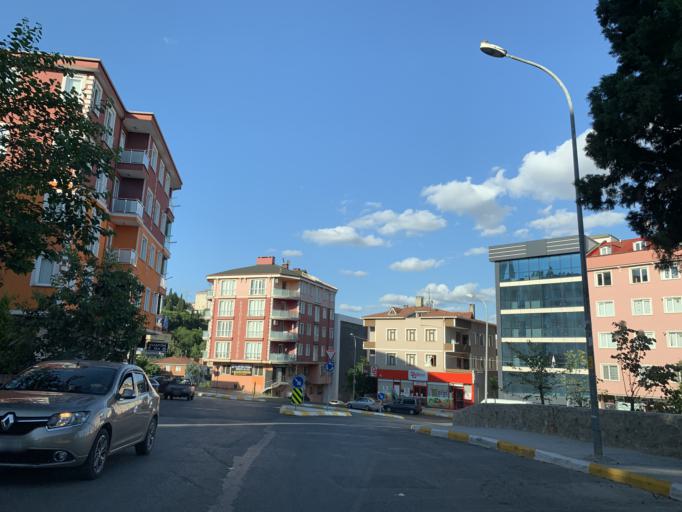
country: TR
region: Istanbul
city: Pendik
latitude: 40.9004
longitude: 29.2557
